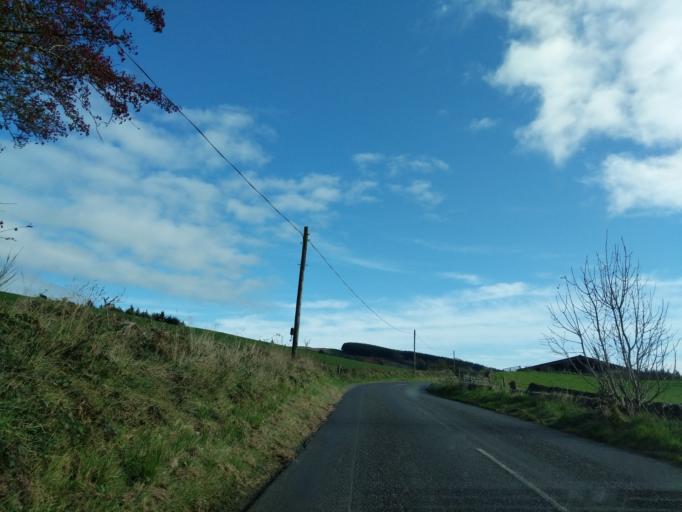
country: GB
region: Scotland
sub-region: Dumfries and Galloway
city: Thornhill
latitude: 55.1917
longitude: -3.8613
